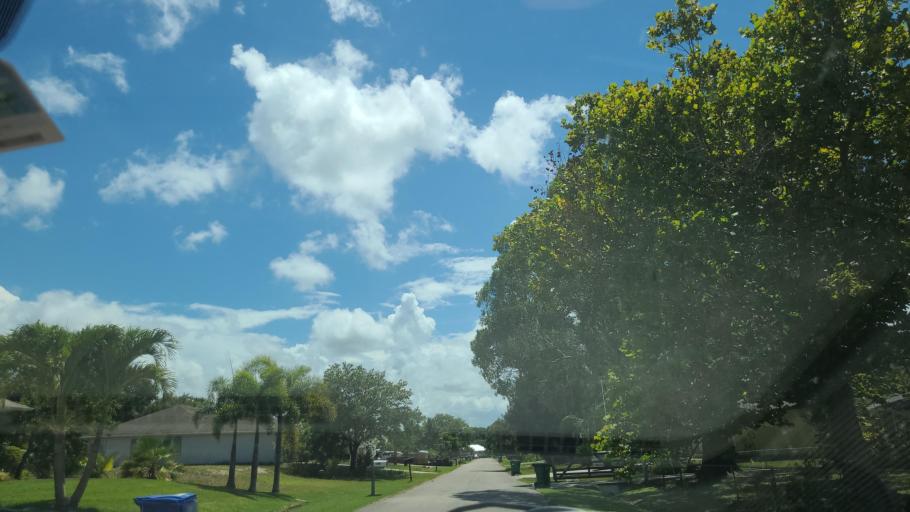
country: US
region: Florida
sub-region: Indian River County
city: Sebastian
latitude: 27.7765
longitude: -80.4800
